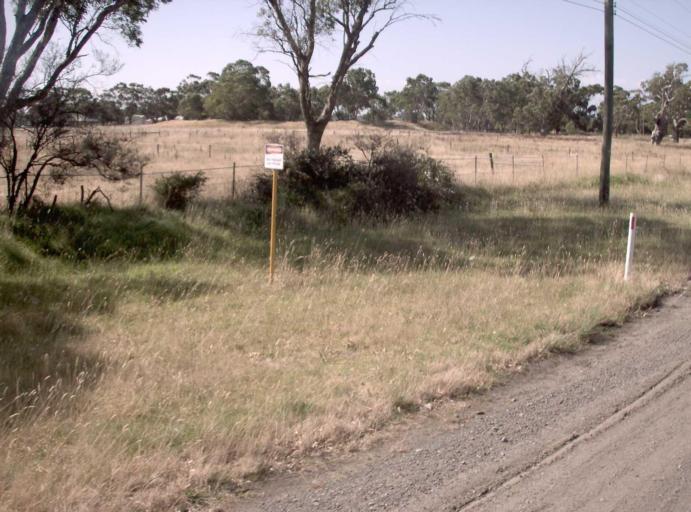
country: AU
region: Victoria
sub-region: Frankston
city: Sandhurst
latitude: -38.0746
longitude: 145.1926
